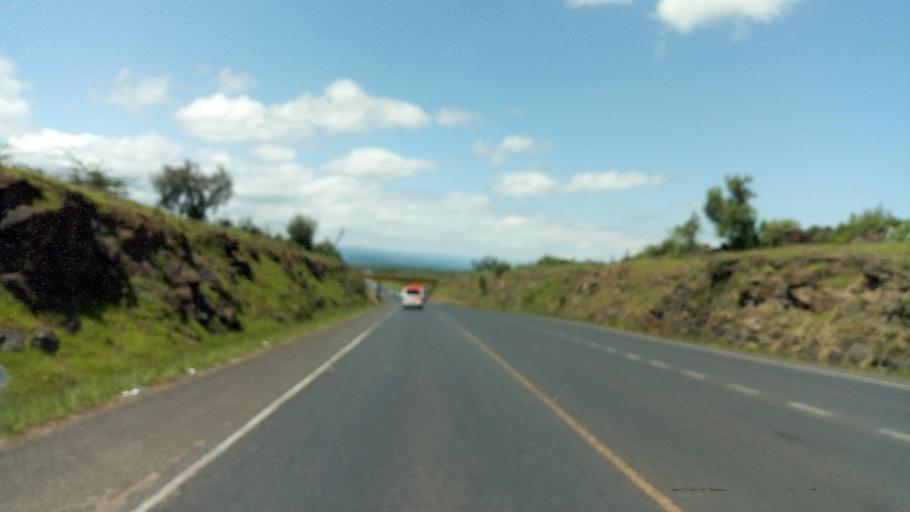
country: KE
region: Nakuru
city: Naivasha
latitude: -0.5421
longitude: 36.3389
